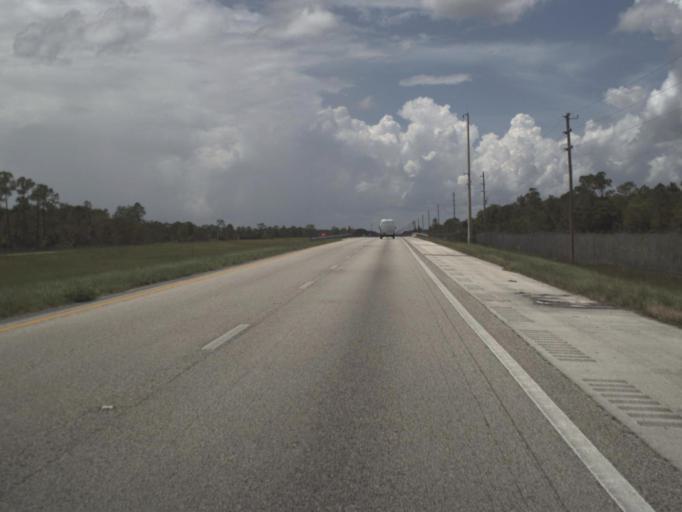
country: US
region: Florida
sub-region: Collier County
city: Immokalee
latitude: 26.1699
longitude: -81.0164
